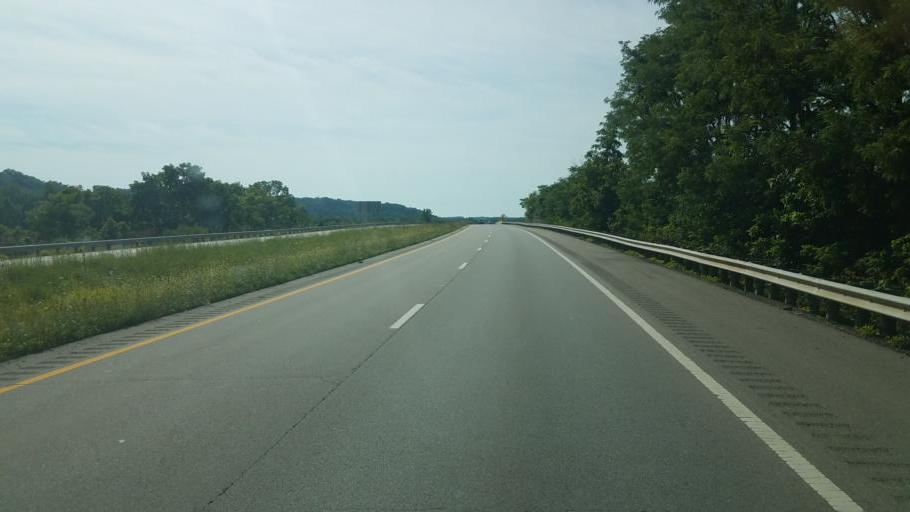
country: US
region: Ohio
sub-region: Hocking County
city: Logan
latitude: 39.4994
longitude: -82.3429
